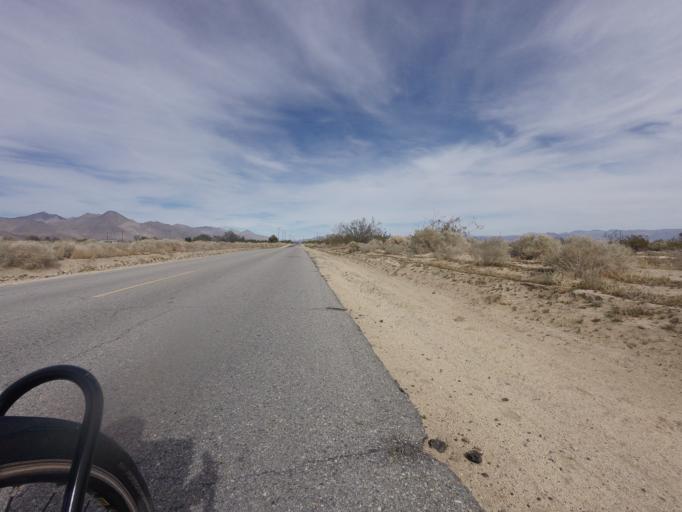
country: US
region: California
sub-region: Kern County
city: Inyokern
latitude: 35.7229
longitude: -117.8349
